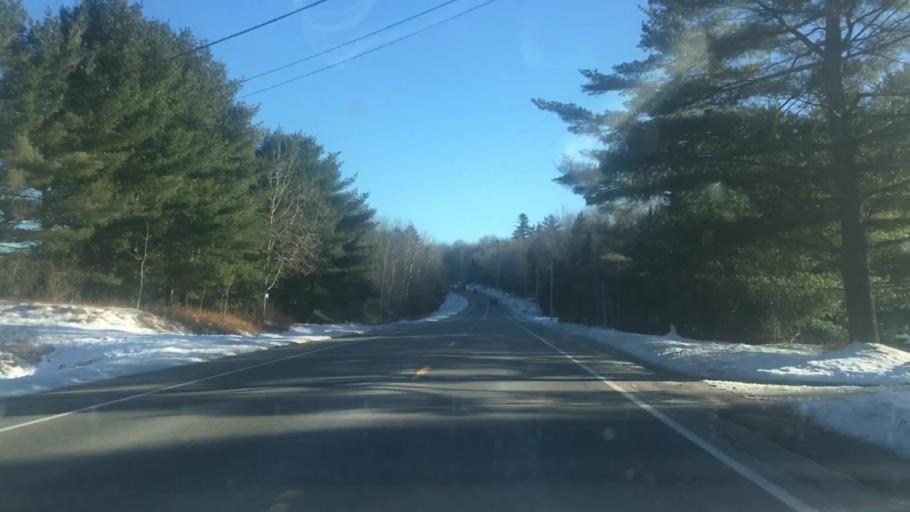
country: US
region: Maine
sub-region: Somerset County
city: Norridgewock
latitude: 44.6733
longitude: -69.7187
